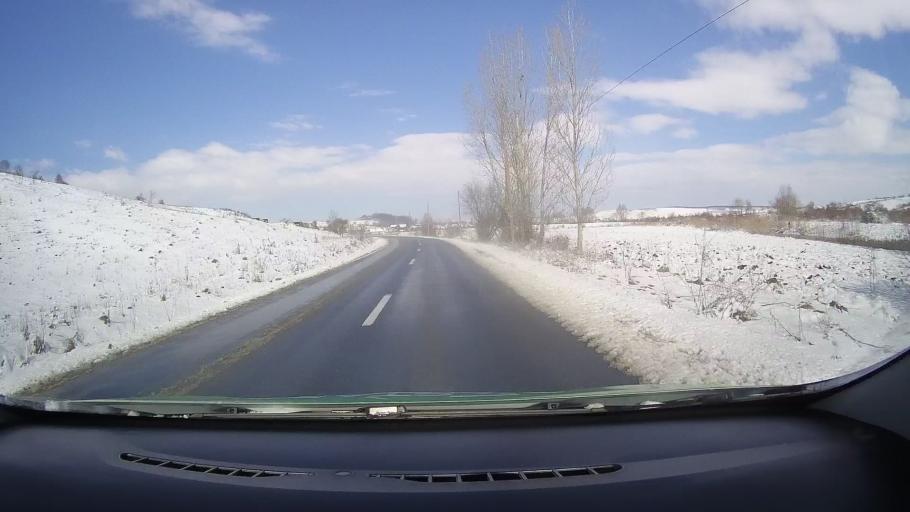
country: RO
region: Sibiu
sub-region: Comuna Nocrich
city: Nocrich
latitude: 45.8809
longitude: 24.4519
